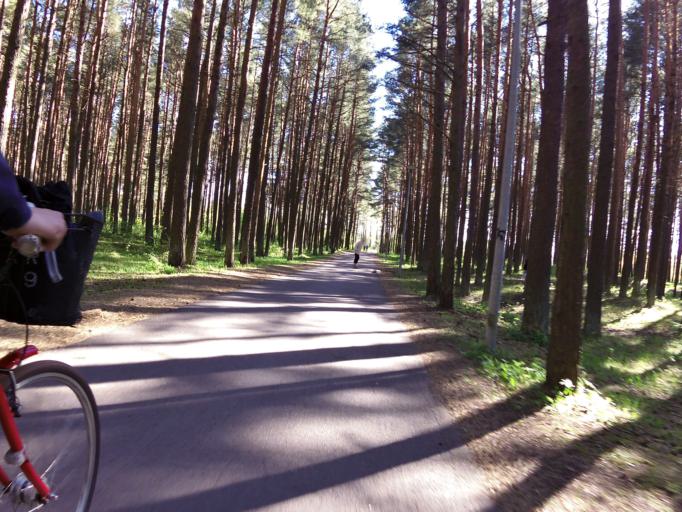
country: EE
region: Harju
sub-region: Viimsi vald
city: Viimsi
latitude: 59.4699
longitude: 24.8309
